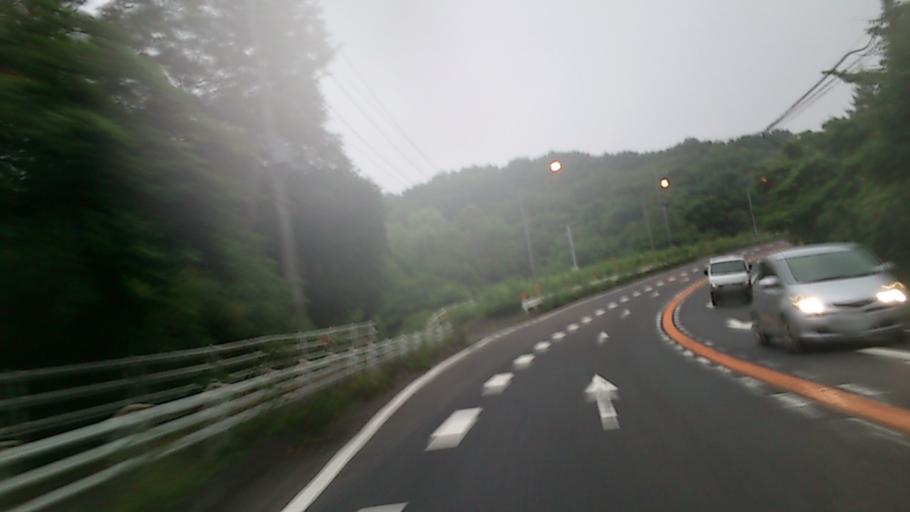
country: JP
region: Tochigi
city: Kuroiso
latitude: 37.0655
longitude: 140.1160
